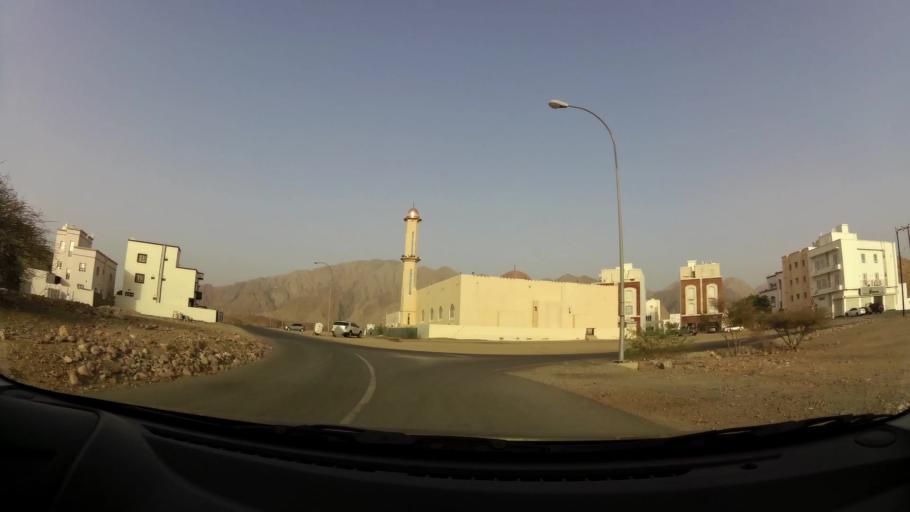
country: OM
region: Muhafazat Masqat
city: Bawshar
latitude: 23.5108
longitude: 58.3453
